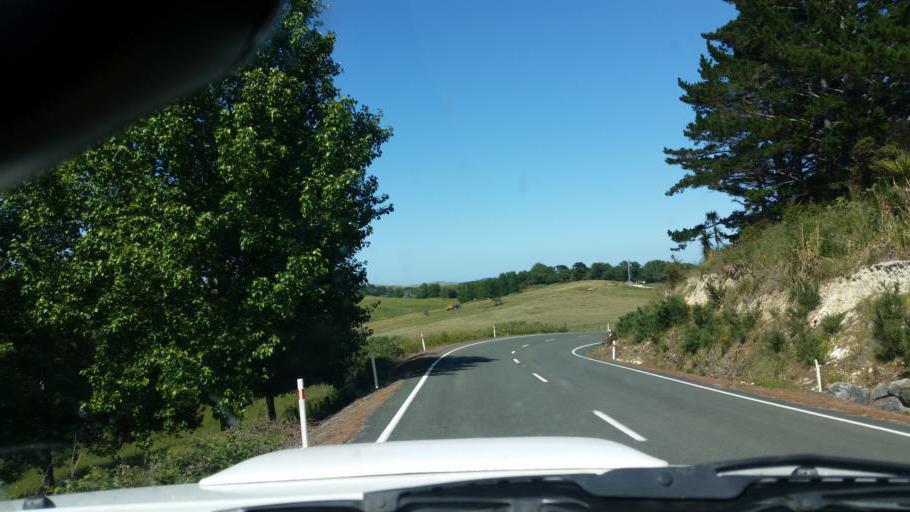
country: NZ
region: Auckland
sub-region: Auckland
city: Wellsford
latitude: -36.2236
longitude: 174.3780
